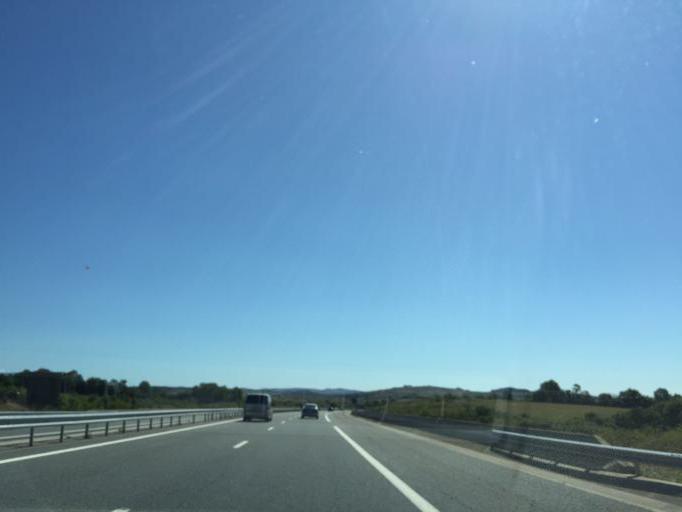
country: FR
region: Midi-Pyrenees
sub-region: Departement de l'Aveyron
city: La Cavalerie
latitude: 43.9990
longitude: 3.1620
